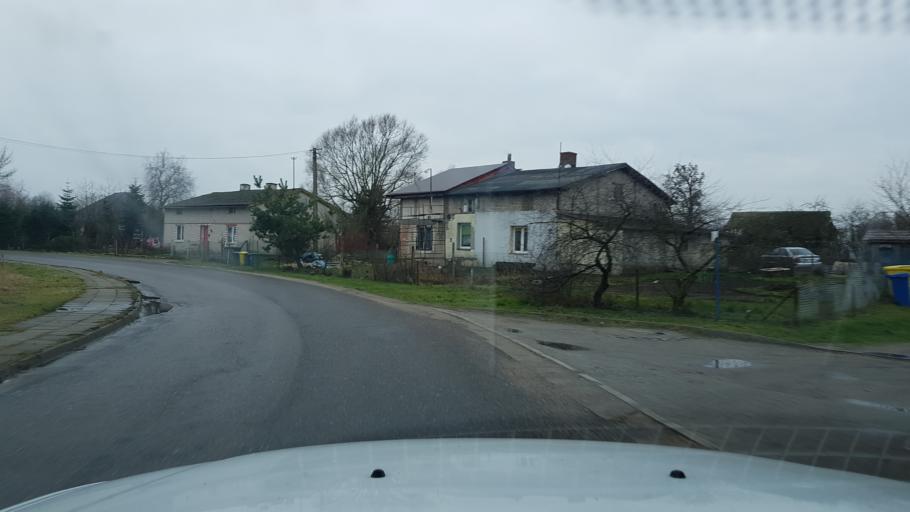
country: PL
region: West Pomeranian Voivodeship
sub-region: Powiat kolobrzeski
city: Grzybowo
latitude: 54.1327
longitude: 15.4780
